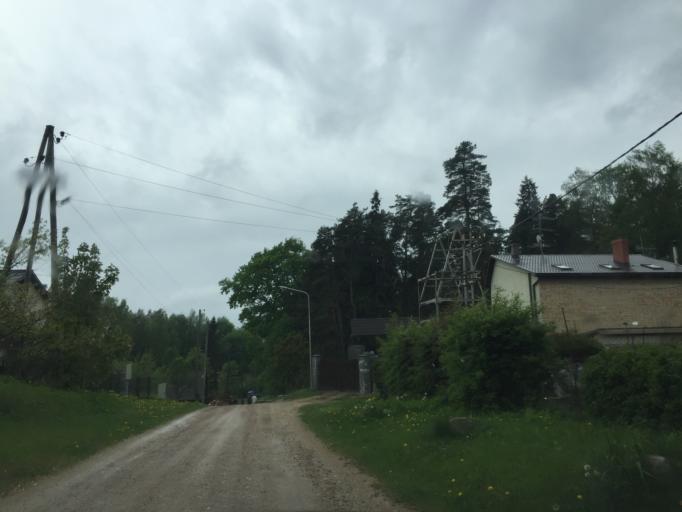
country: LV
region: Kegums
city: Kegums
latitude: 56.7477
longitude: 24.7315
